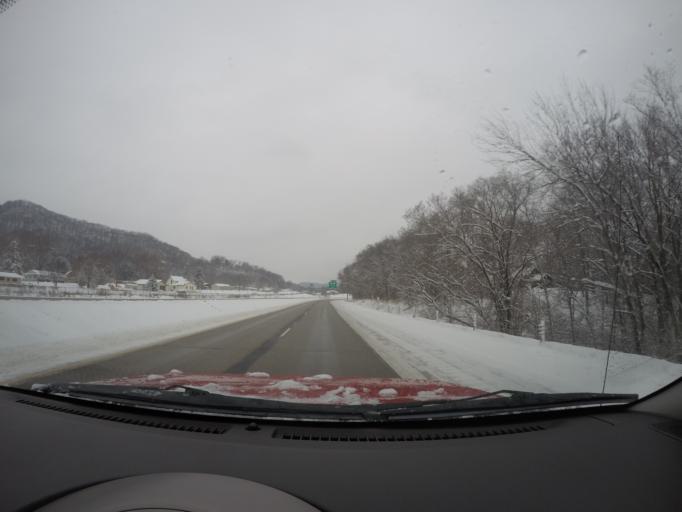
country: US
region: Wisconsin
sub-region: La Crosse County
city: Brice Prairie
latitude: 43.9087
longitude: -91.3563
